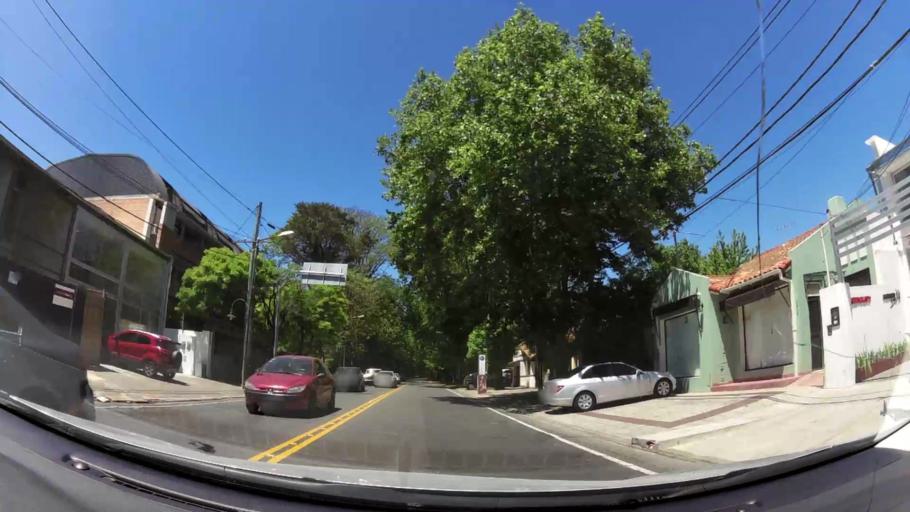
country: AR
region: Buenos Aires
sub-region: Partido de San Isidro
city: San Isidro
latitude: -34.4474
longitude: -58.5416
